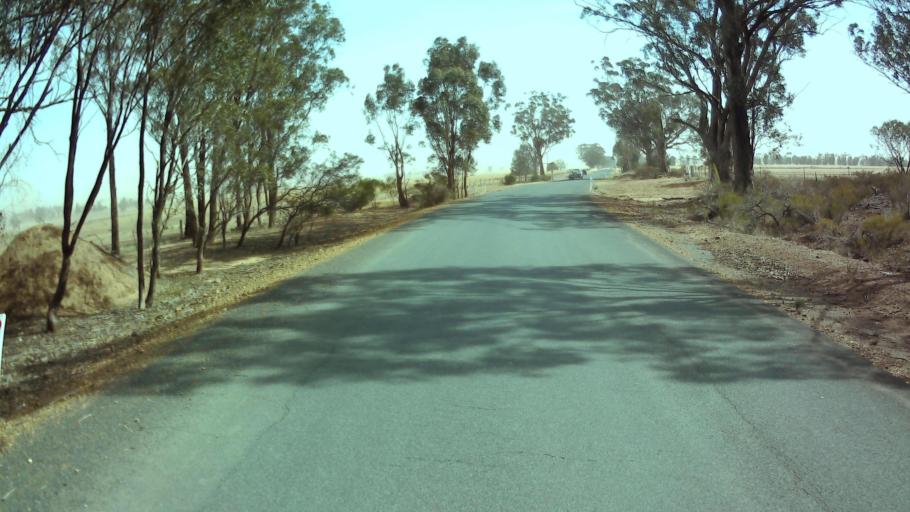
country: AU
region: New South Wales
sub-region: Weddin
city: Grenfell
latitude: -33.7737
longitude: 147.9863
